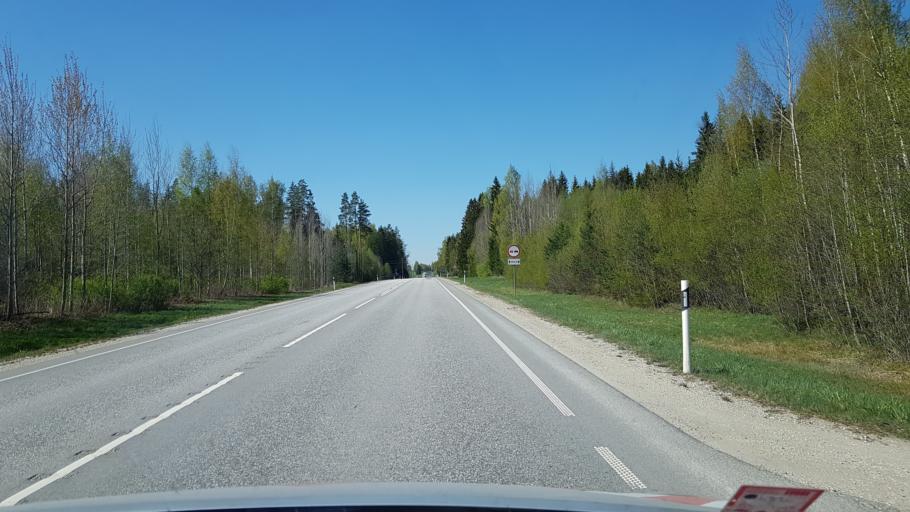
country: EE
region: Vorumaa
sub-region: Antsla vald
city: Vana-Antsla
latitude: 57.9727
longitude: 26.7829
